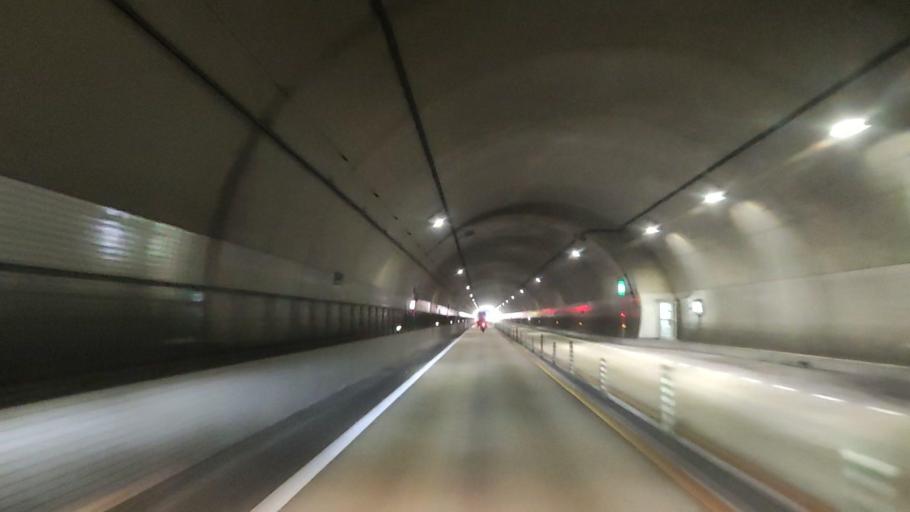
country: JP
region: Shizuoka
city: Ito
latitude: 34.9347
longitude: 138.9413
